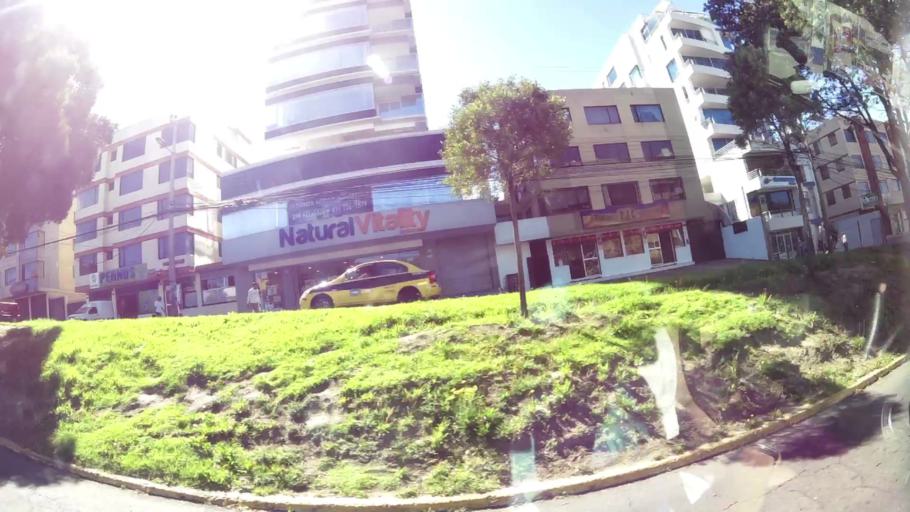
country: EC
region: Pichincha
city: Quito
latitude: -0.1399
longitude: -78.4701
